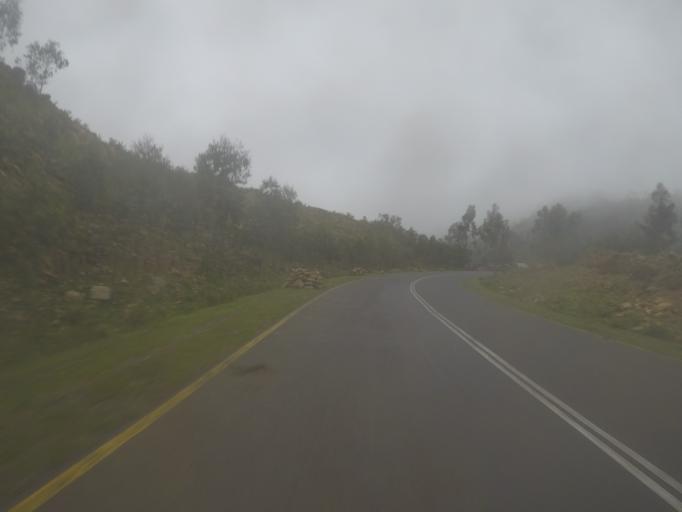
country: ET
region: Amhara
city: Gondar
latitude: 12.7478
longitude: 37.5276
